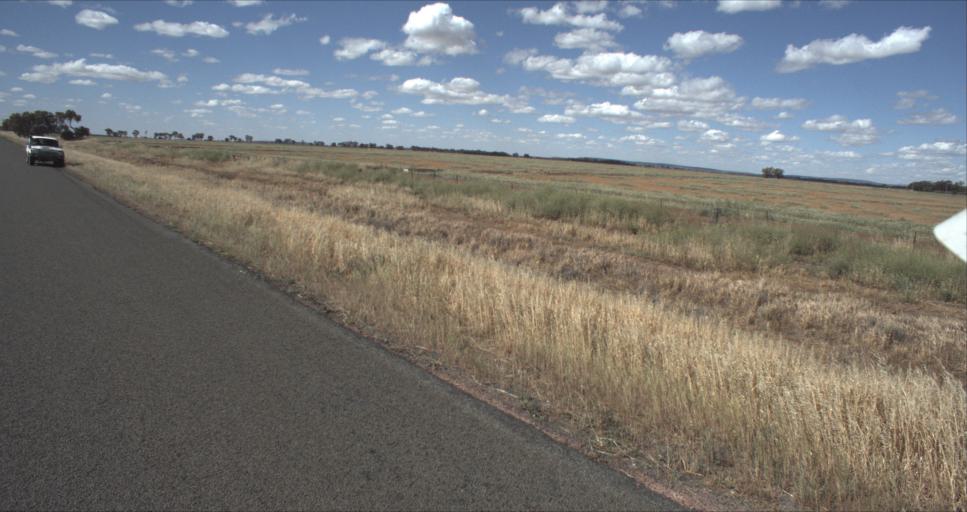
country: AU
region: New South Wales
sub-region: Leeton
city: Leeton
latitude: -34.4700
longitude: 146.2511
